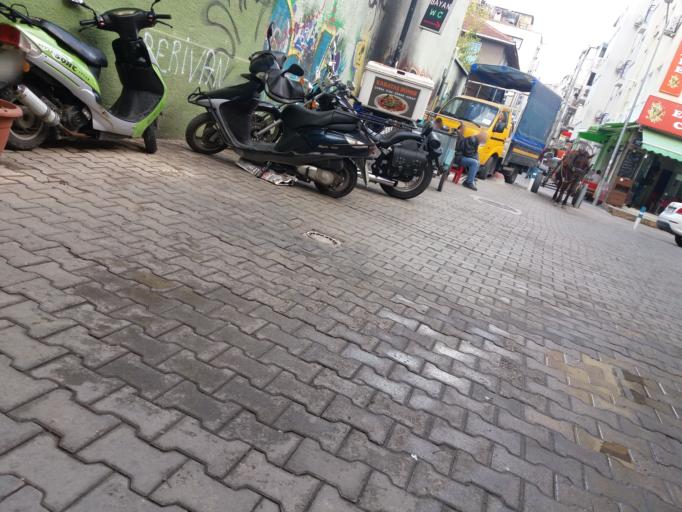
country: TR
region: Izmir
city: Izmir
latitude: 38.4370
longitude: 27.1435
